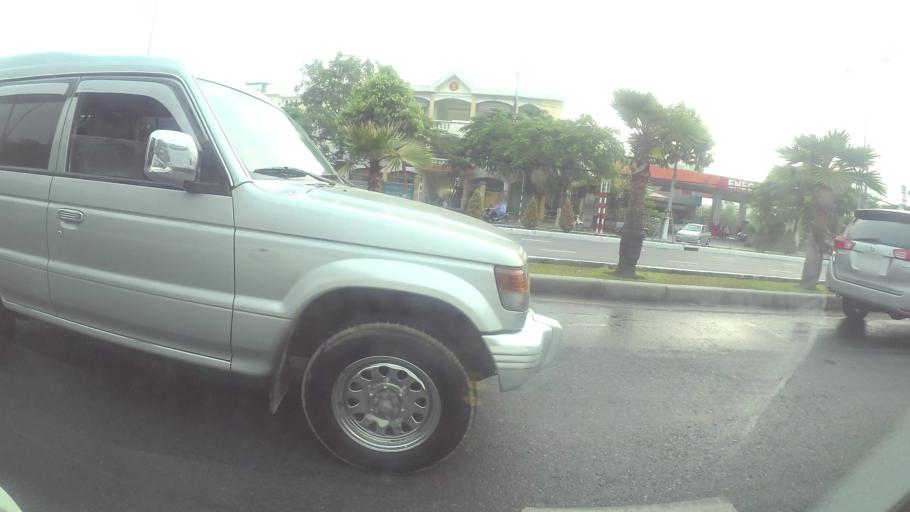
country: VN
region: Da Nang
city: Son Tra
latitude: 16.0451
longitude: 108.2395
